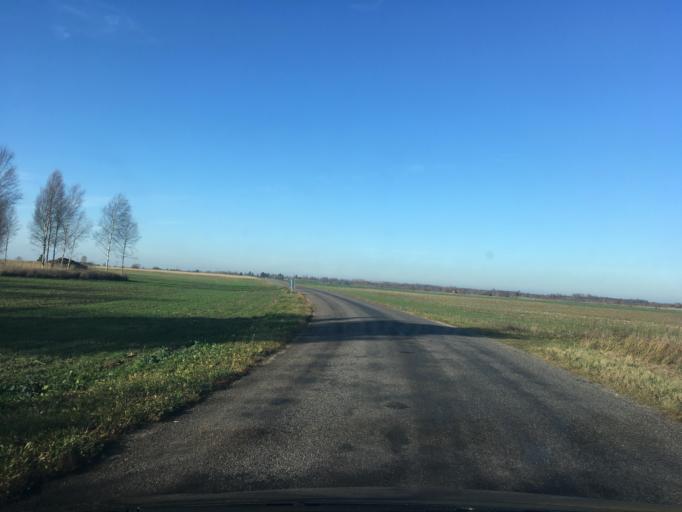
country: EE
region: Harju
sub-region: Raasiku vald
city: Arukula
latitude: 59.4500
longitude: 25.1166
